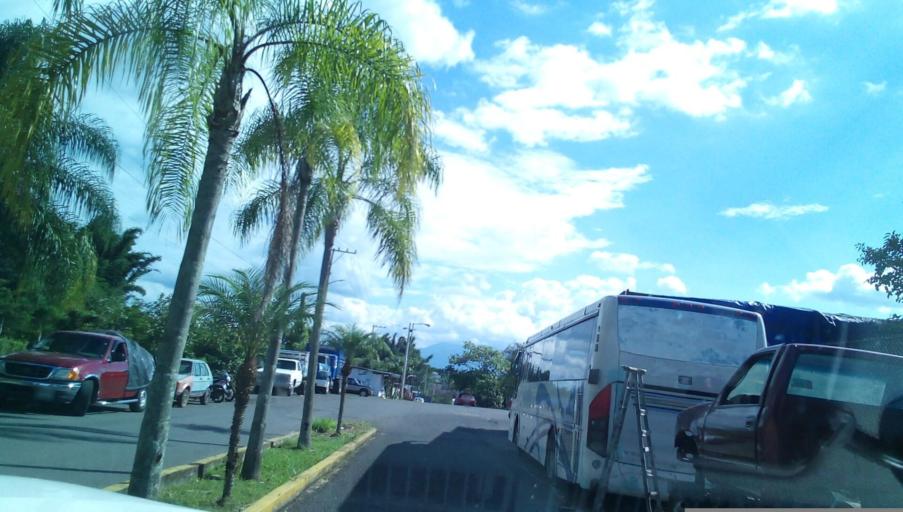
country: MX
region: Veracruz
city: Cordoba
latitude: 18.8896
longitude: -96.9204
